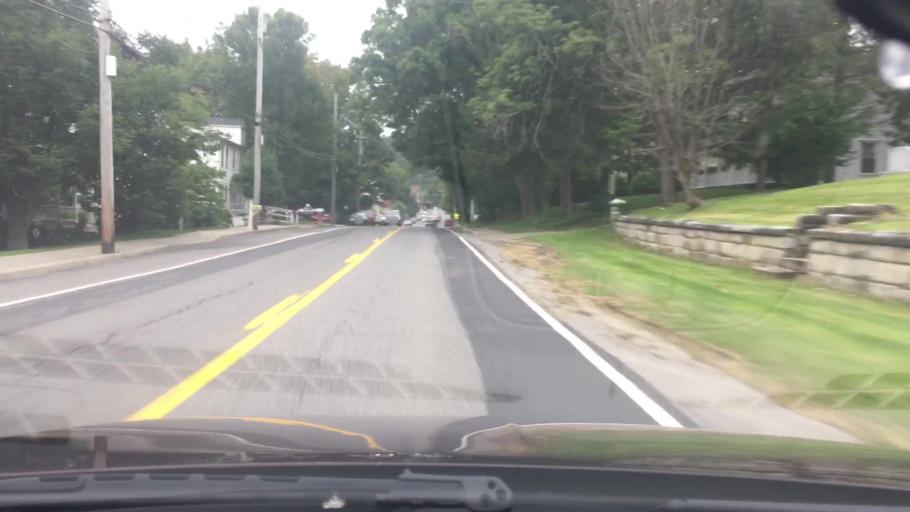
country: US
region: New York
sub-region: Dutchess County
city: Dover Plains
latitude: 41.8508
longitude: -73.5513
